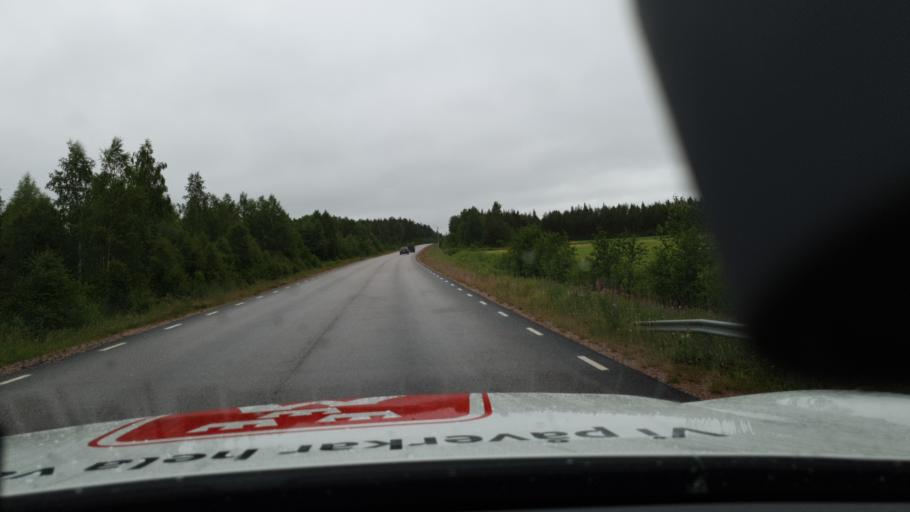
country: SE
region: Norrbotten
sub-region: Overtornea Kommun
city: OEvertornea
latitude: 66.5097
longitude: 23.7284
